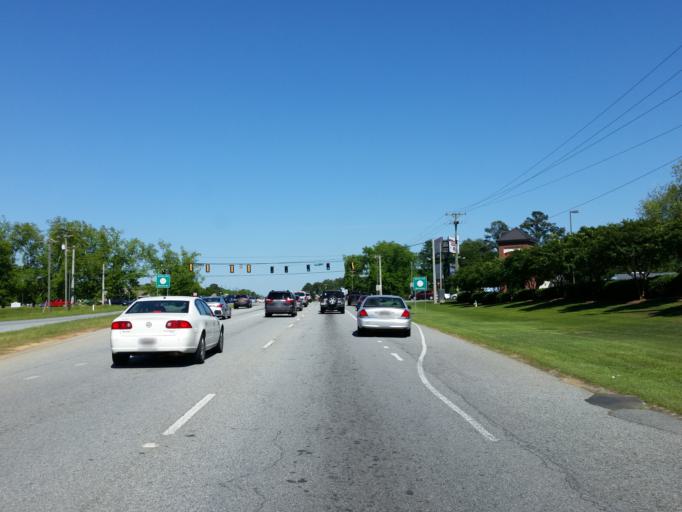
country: US
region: Georgia
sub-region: Lowndes County
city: Valdosta
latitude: 30.8828
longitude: -83.2749
